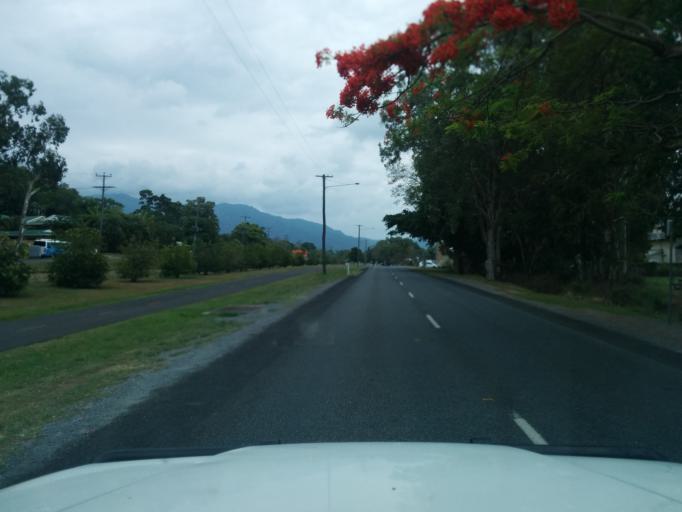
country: AU
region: Queensland
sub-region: Cairns
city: Redlynch
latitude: -16.8746
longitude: 145.7386
